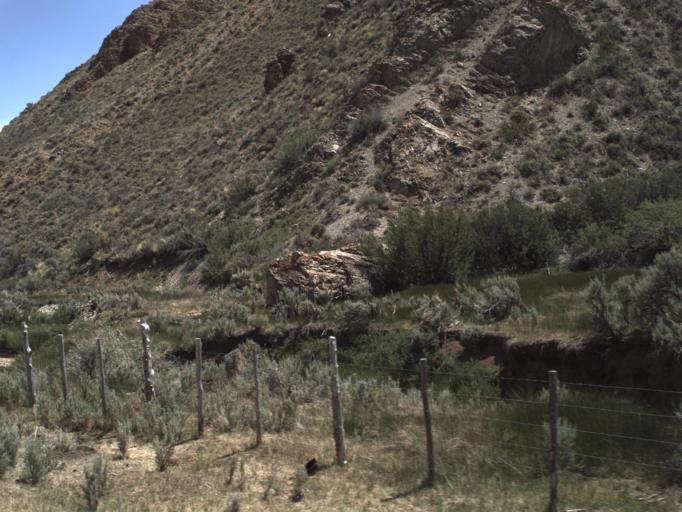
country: US
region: Utah
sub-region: Rich County
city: Randolph
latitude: 41.5038
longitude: -111.2898
